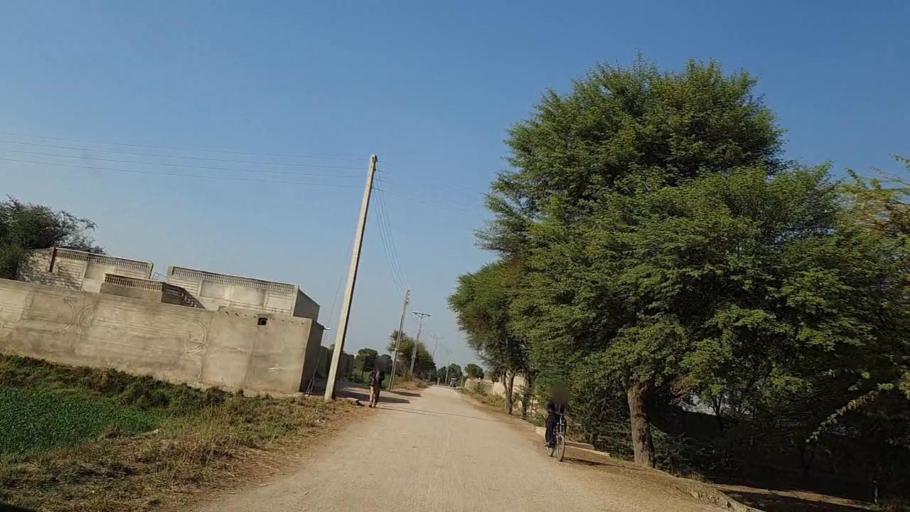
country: PK
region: Sindh
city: Sakrand
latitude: 26.1305
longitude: 68.2378
